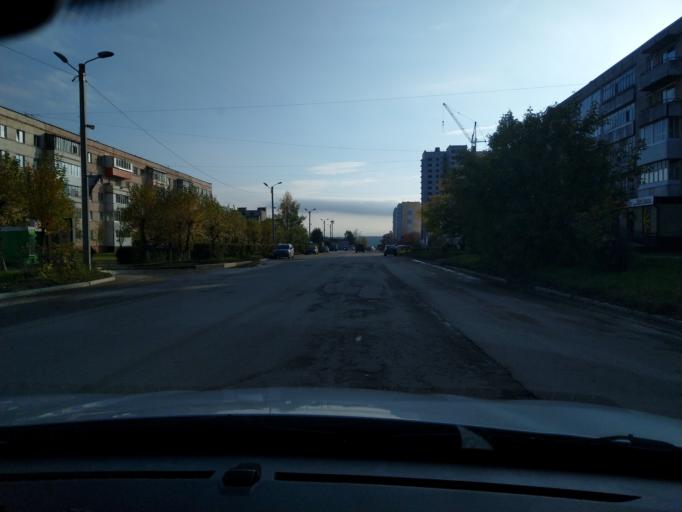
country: RU
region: Perm
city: Dobryanka
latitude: 58.4647
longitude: 56.4013
